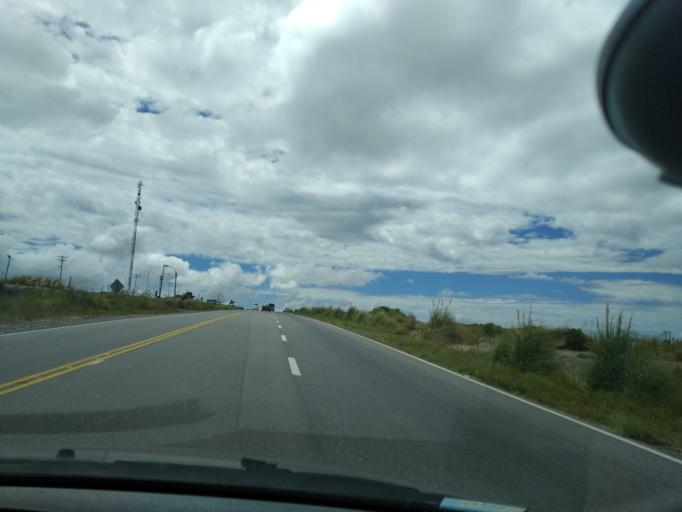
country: AR
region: Cordoba
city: Mina Clavero
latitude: -31.6172
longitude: -64.8763
